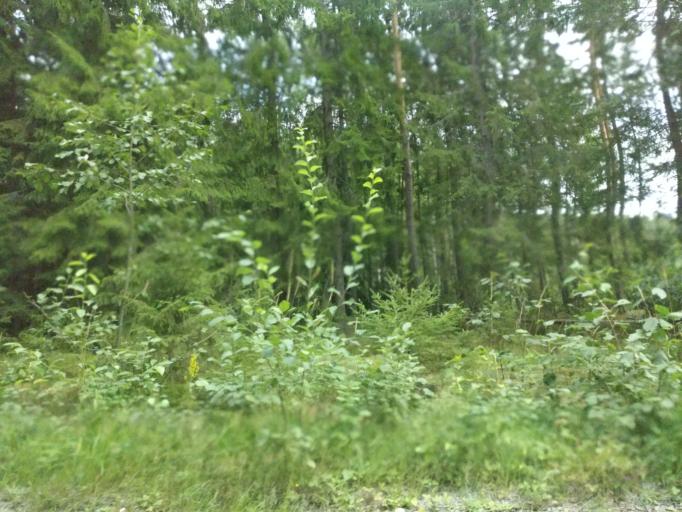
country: SE
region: Vaermland
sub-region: Hagfors Kommun
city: Hagfors
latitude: 60.0049
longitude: 13.7268
